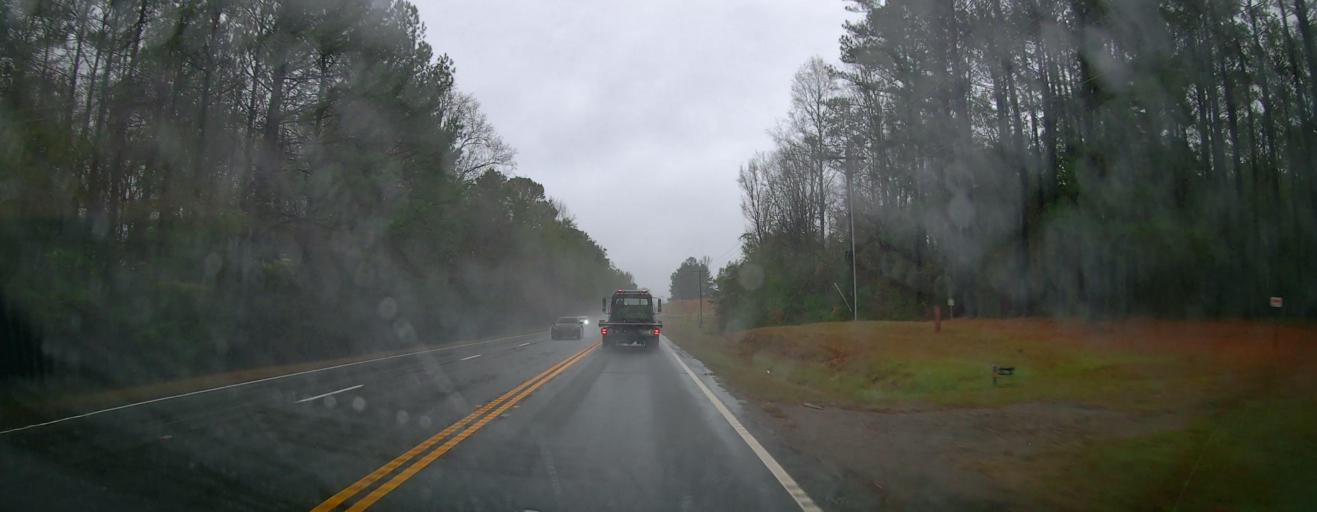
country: US
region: Georgia
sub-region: Jones County
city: Gray
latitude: 33.0488
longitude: -83.5077
